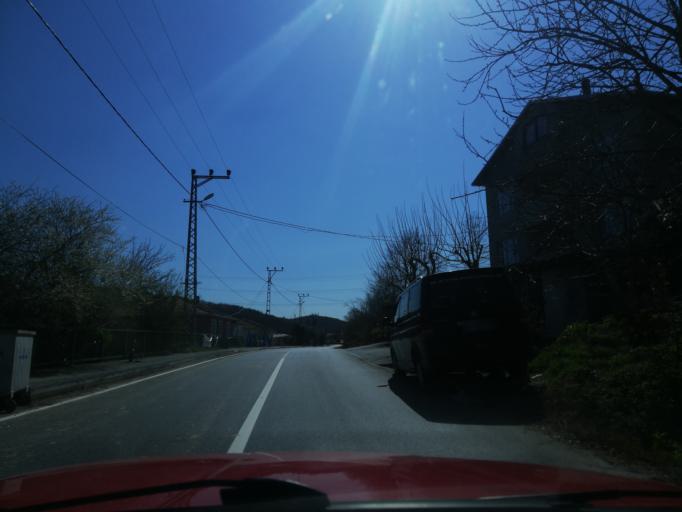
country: TR
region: Istanbul
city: Mahmut Sevket Pasa
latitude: 41.1323
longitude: 29.1634
